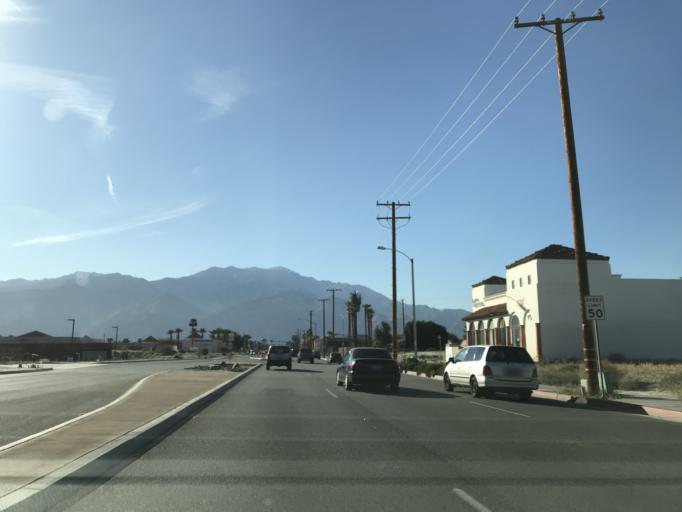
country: US
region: California
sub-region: Riverside County
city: Cathedral City
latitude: 33.8160
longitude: -116.4526
